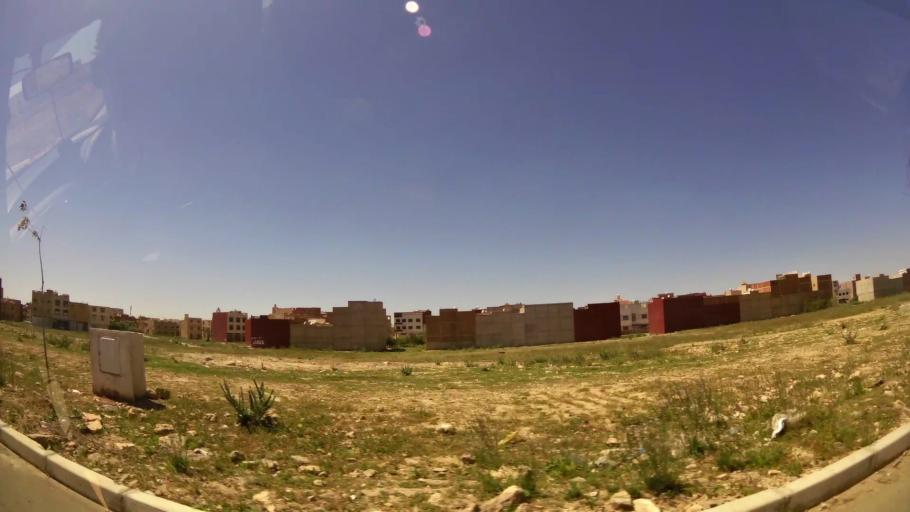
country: MA
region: Oriental
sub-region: Oujda-Angad
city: Oujda
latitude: 34.6689
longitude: -1.8674
